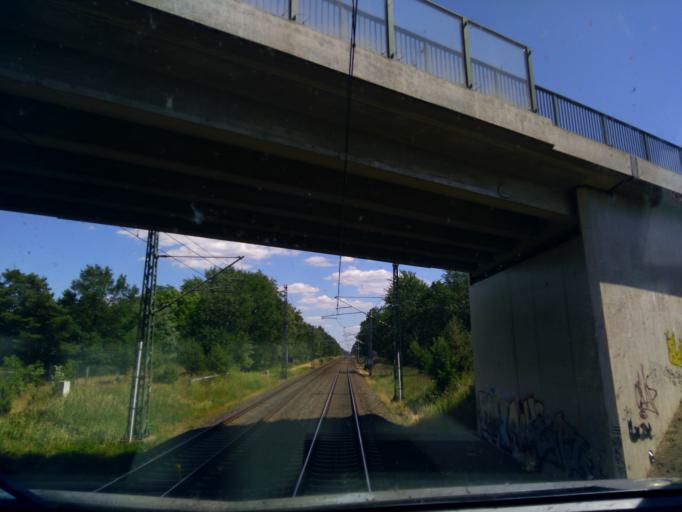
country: DE
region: Brandenburg
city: Ruhstadt
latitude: 52.9851
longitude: 11.8697
